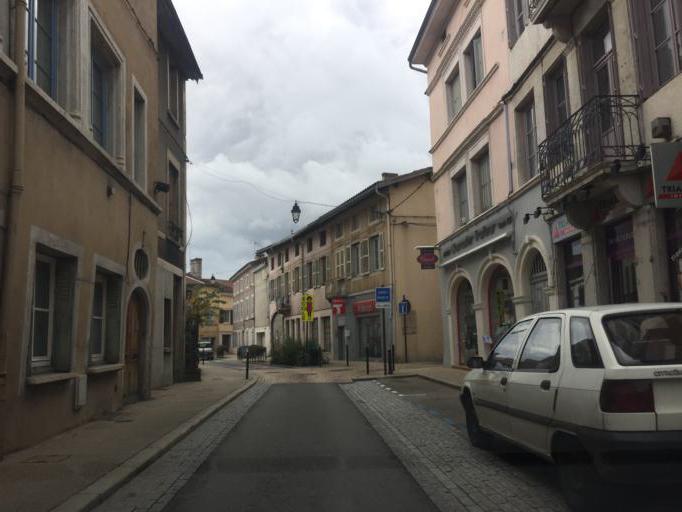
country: FR
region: Rhone-Alpes
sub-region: Departement de l'Ain
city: Montluel
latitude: 45.8510
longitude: 5.0554
